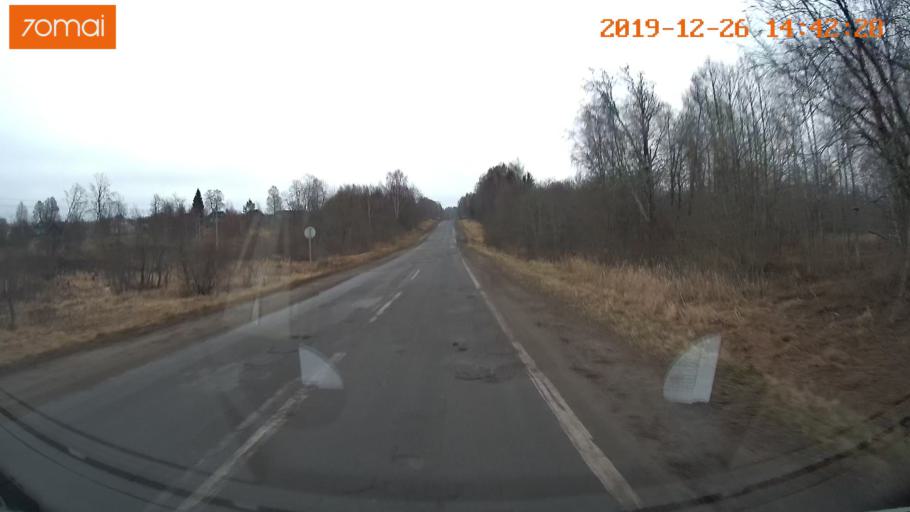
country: RU
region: Jaroslavl
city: Poshekhon'ye
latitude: 58.3639
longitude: 39.0303
